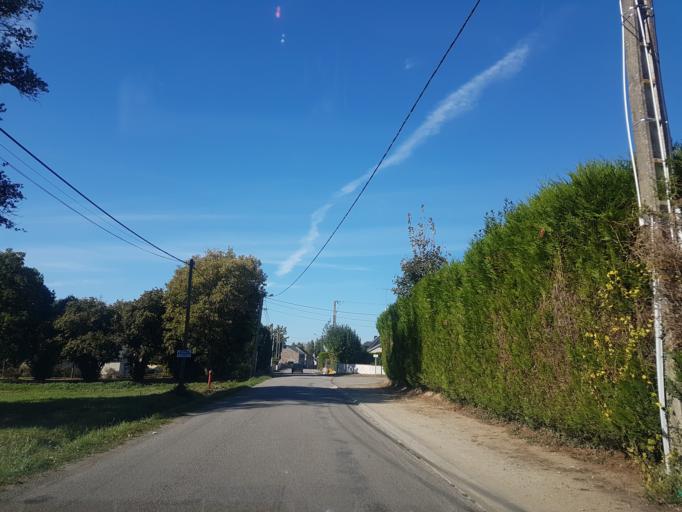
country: FR
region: Pays de la Loire
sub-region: Departement de la Loire-Atlantique
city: Petit-Mars
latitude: 47.3947
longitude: -1.4599
